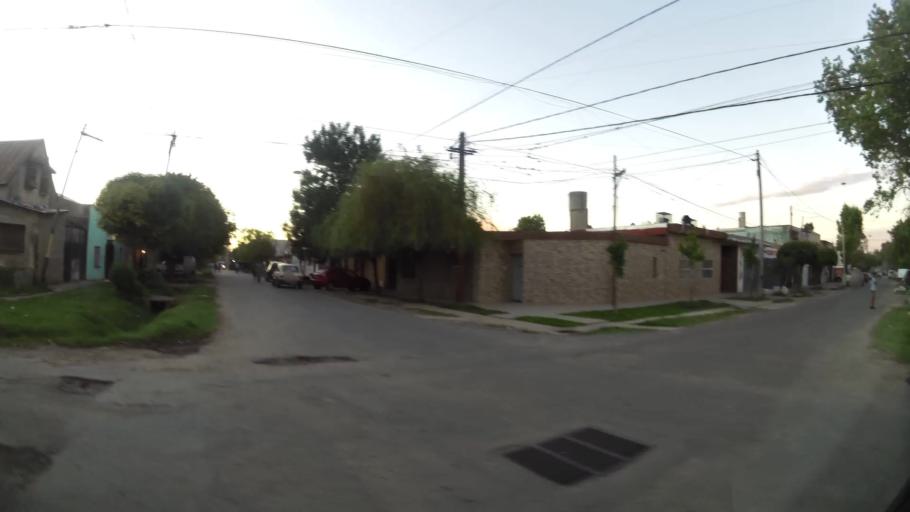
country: AR
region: Santa Fe
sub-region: Departamento de Rosario
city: Rosario
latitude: -32.9632
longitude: -60.6880
